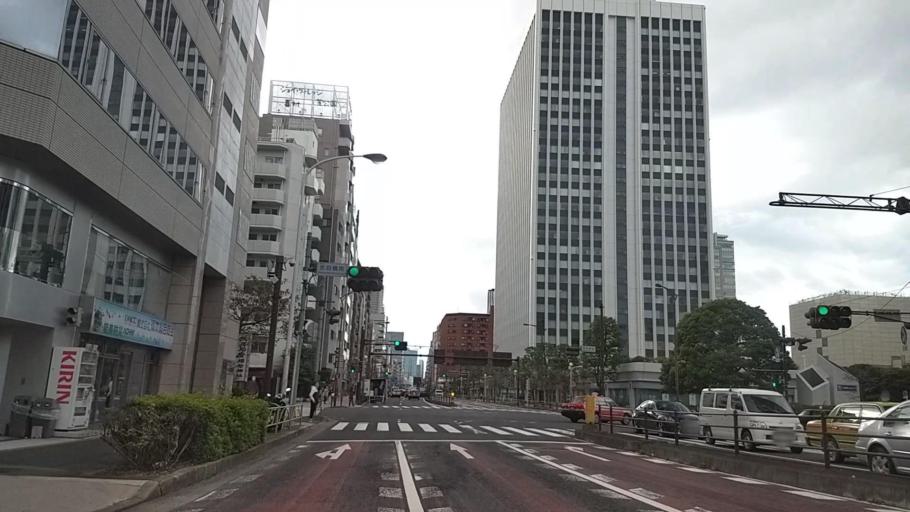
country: JP
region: Tokyo
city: Tokyo
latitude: 35.6544
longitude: 139.7453
